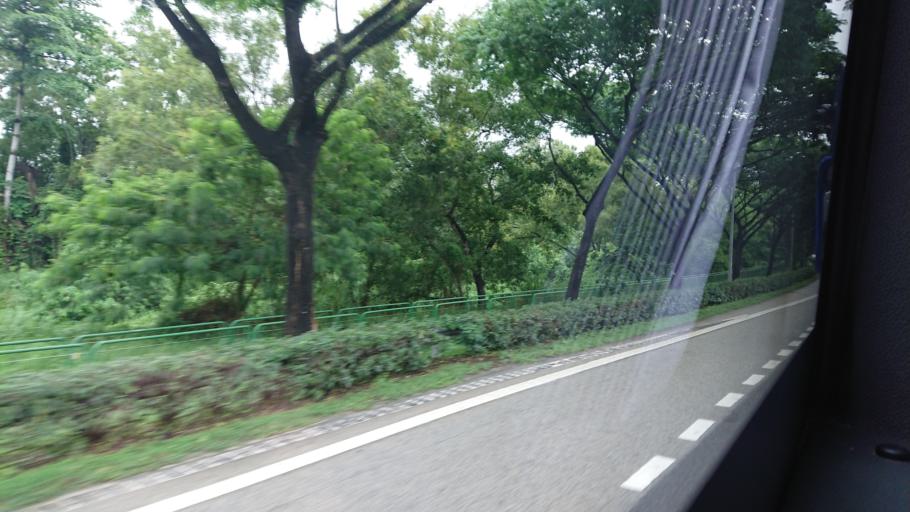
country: MY
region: Johor
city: Kampung Pasir Gudang Baru
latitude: 1.3799
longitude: 103.9208
